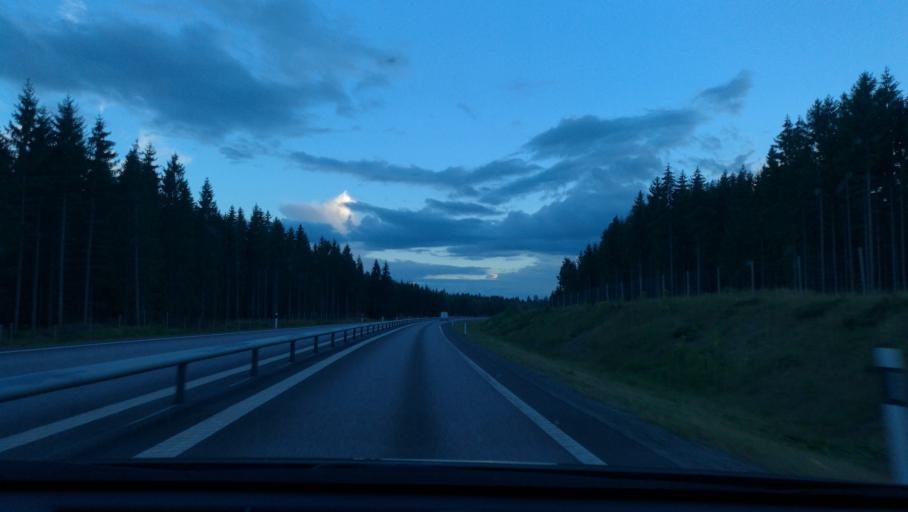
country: SE
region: Soedermanland
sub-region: Katrineholms Kommun
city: Katrineholm
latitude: 58.9439
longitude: 16.2138
